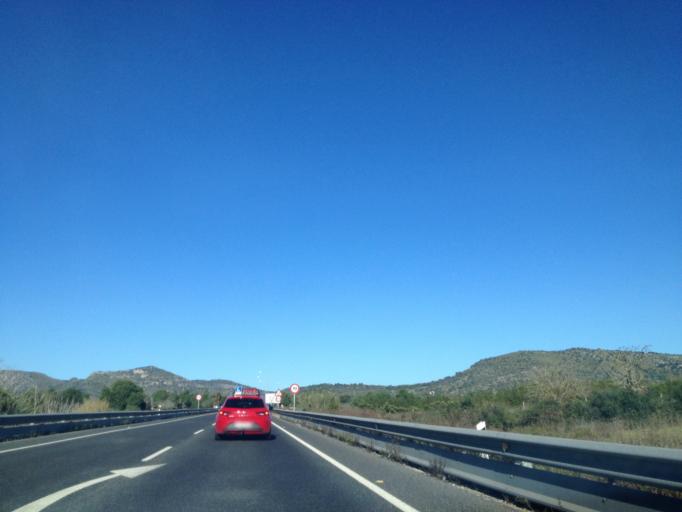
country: ES
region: Balearic Islands
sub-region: Illes Balears
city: Sant Llorenc des Cardassar
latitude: 39.6128
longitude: 3.2961
